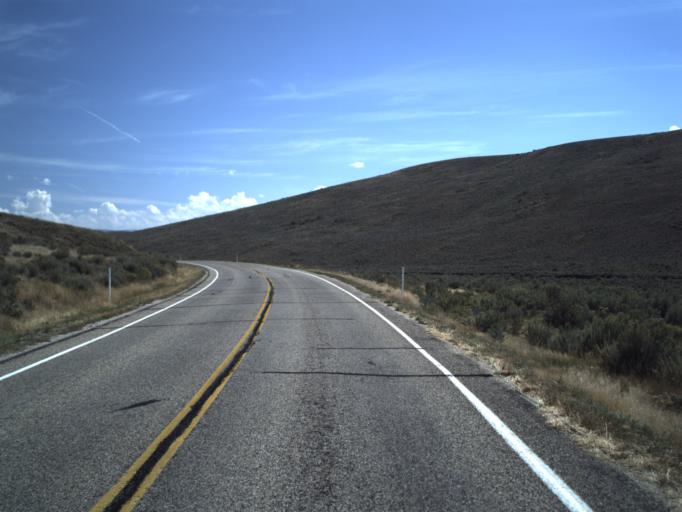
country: US
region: Utah
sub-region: Rich County
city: Randolph
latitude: 41.7695
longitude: -111.1731
